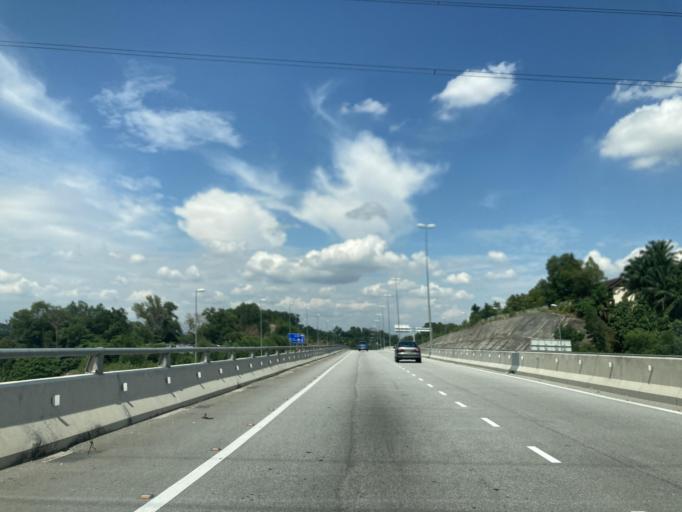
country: MY
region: Selangor
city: Kampung Baru Subang
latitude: 3.1266
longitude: 101.5203
